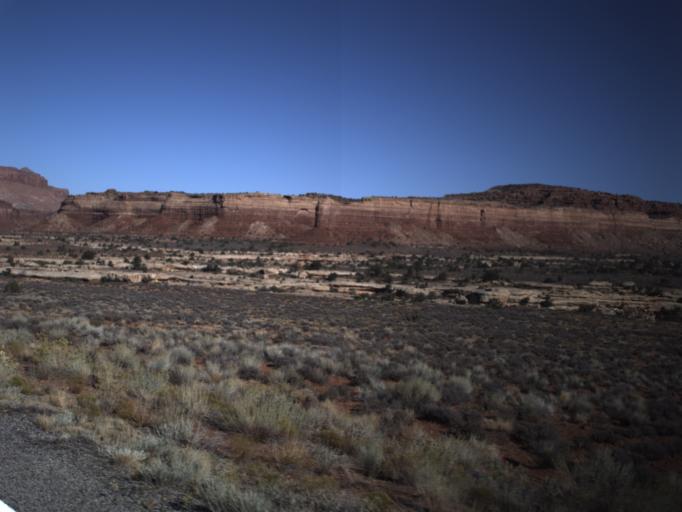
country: US
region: Utah
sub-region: San Juan County
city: Blanding
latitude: 37.7302
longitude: -110.2513
